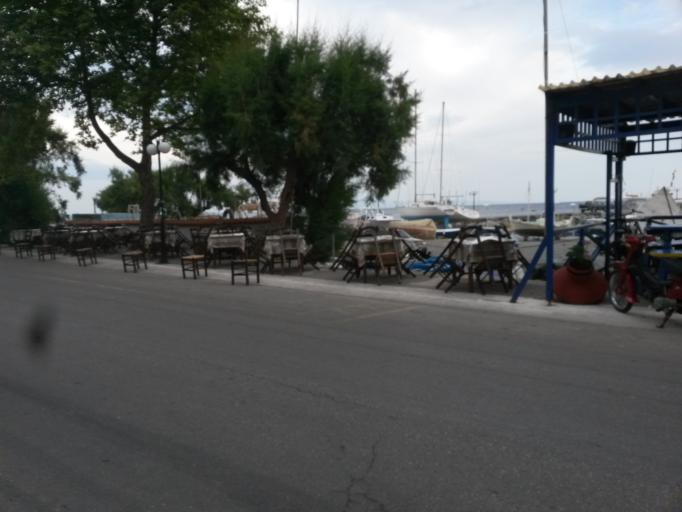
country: GR
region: North Aegean
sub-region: Nomos Lesvou
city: Plomarion
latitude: 38.9744
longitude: 26.3714
